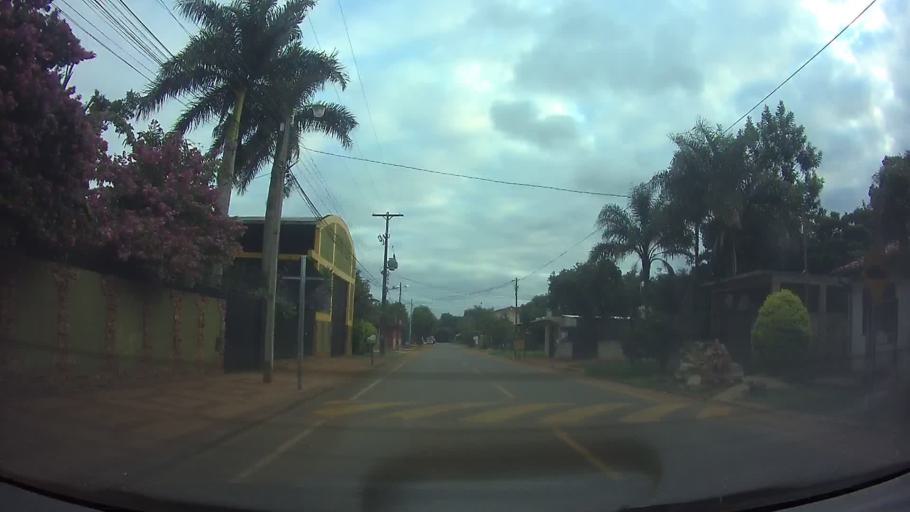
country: PY
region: Central
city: San Lorenzo
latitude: -25.2845
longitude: -57.4867
